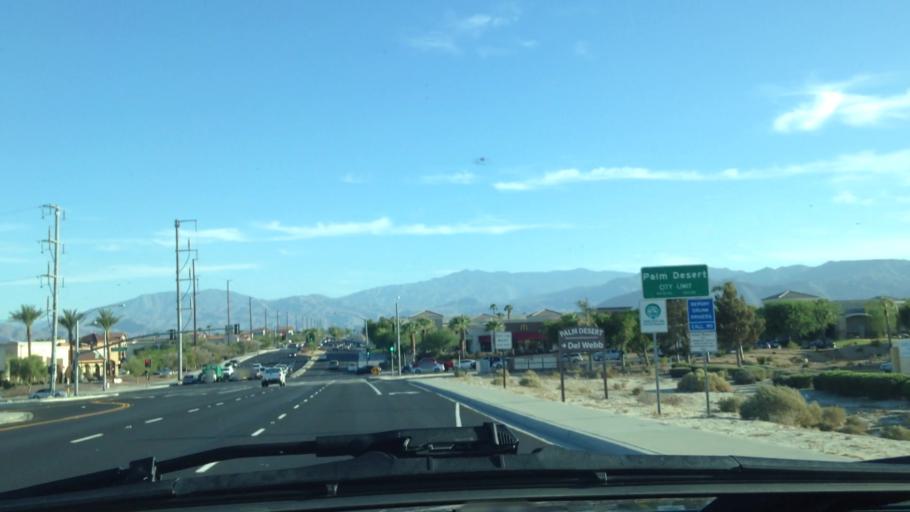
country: US
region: California
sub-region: Riverside County
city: Thousand Palms
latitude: 33.8031
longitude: -116.3884
